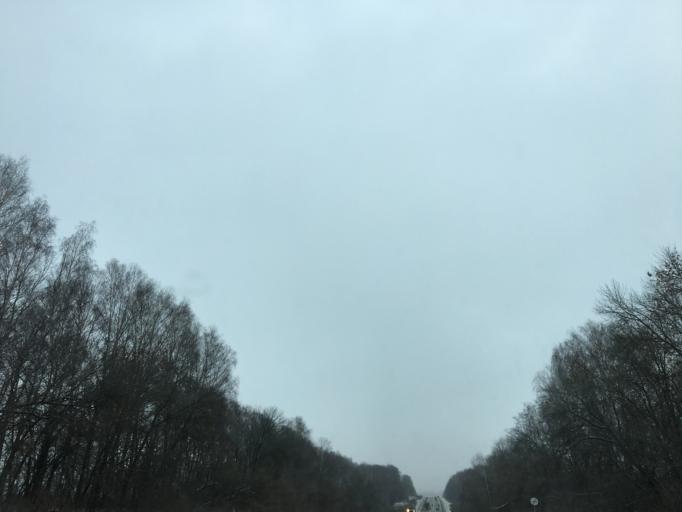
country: RU
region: Tula
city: Bolokhovo
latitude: 54.0451
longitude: 37.8546
